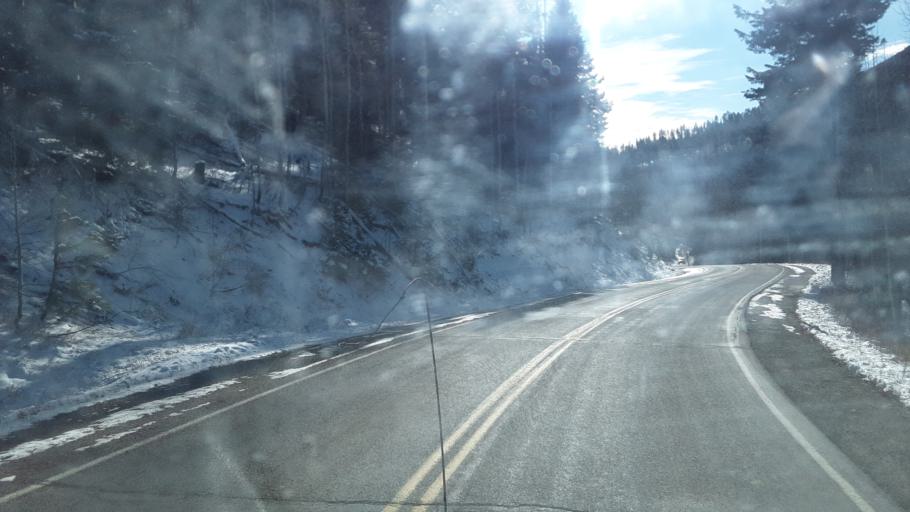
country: US
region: Colorado
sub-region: La Plata County
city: Bayfield
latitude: 37.3741
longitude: -107.6604
